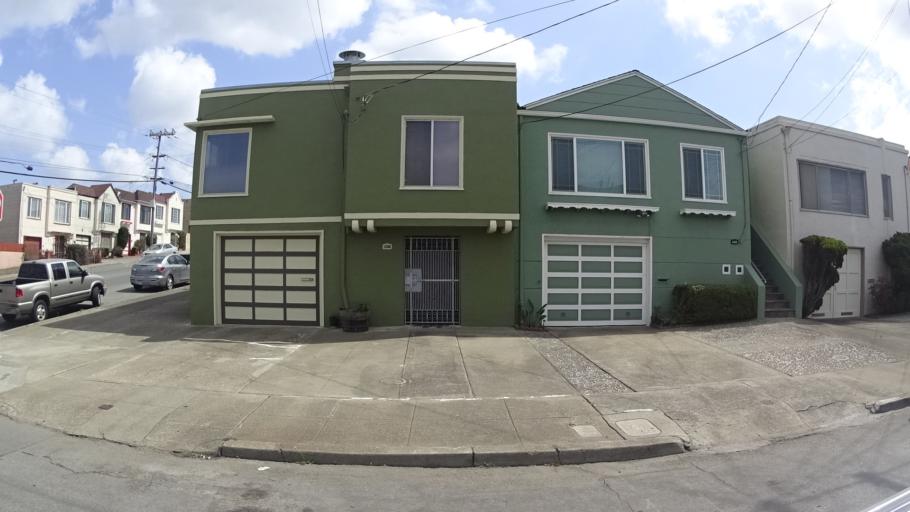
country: US
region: California
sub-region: San Mateo County
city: Daly City
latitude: 37.7456
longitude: -122.4995
